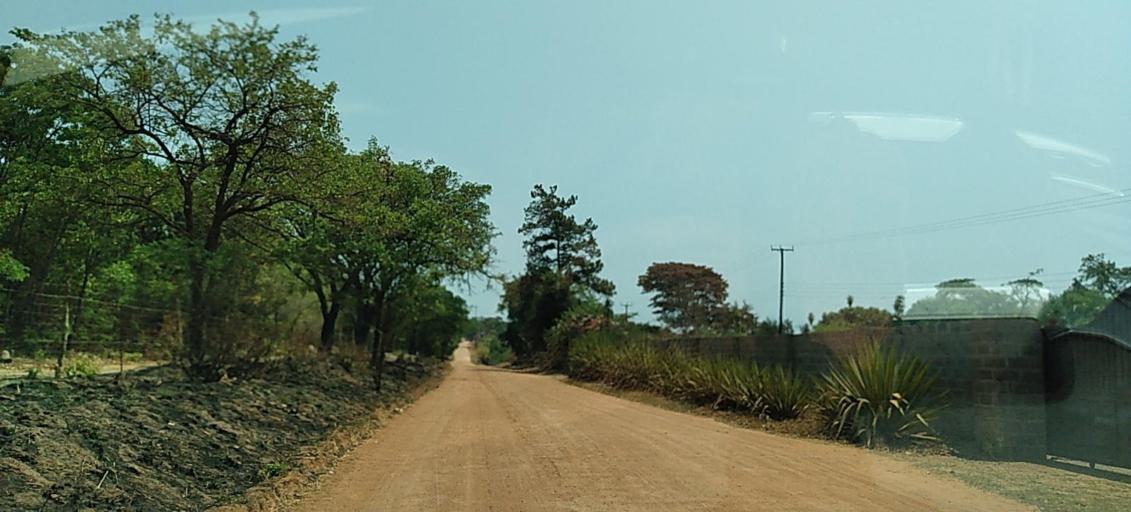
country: ZM
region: Copperbelt
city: Chambishi
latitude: -12.6106
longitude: 27.9522
